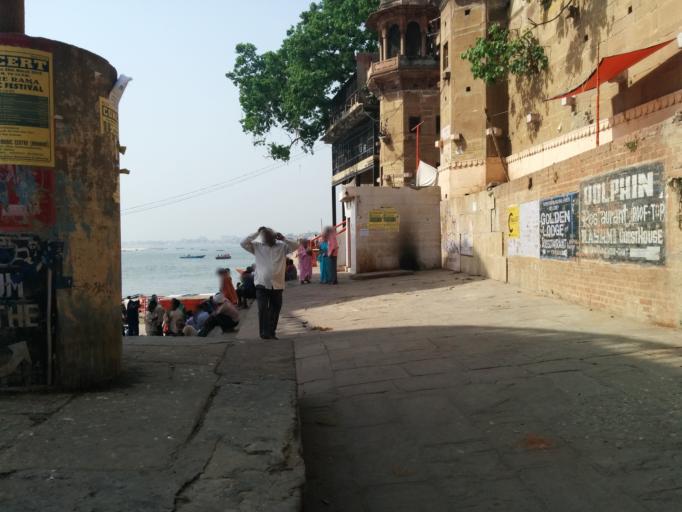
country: IN
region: Uttar Pradesh
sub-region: Varanasi
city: Varanasi
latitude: 25.3103
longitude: 83.0134
